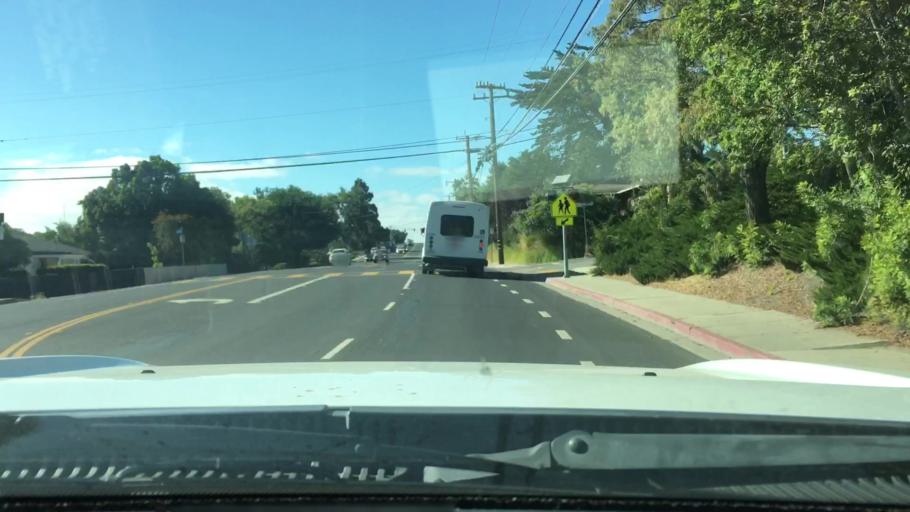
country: US
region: California
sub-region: San Luis Obispo County
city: San Luis Obispo
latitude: 35.2713
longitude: -120.6436
